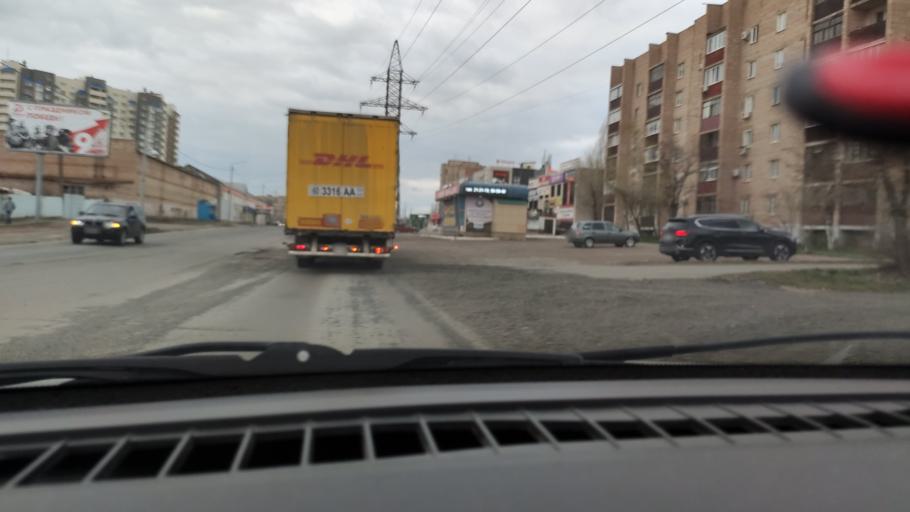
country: RU
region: Orenburg
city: Orenburg
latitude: 51.7859
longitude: 55.1739
